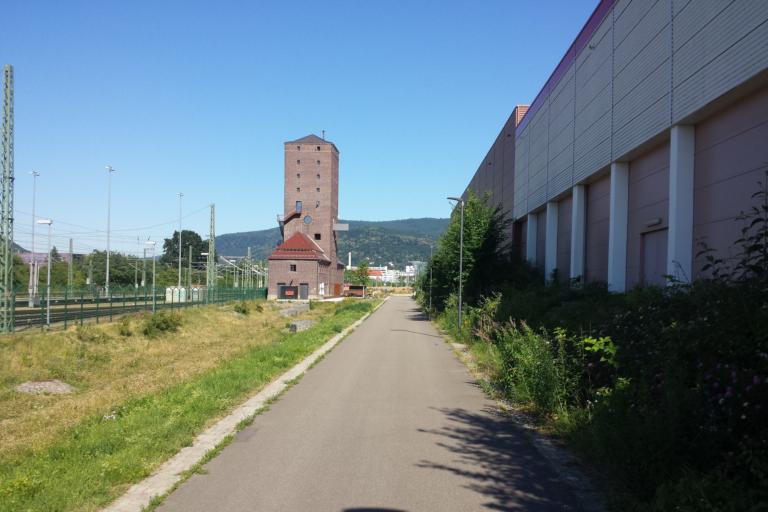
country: DE
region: Baden-Wuerttemberg
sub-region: Karlsruhe Region
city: Eppelheim
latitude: 49.4079
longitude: 8.6574
